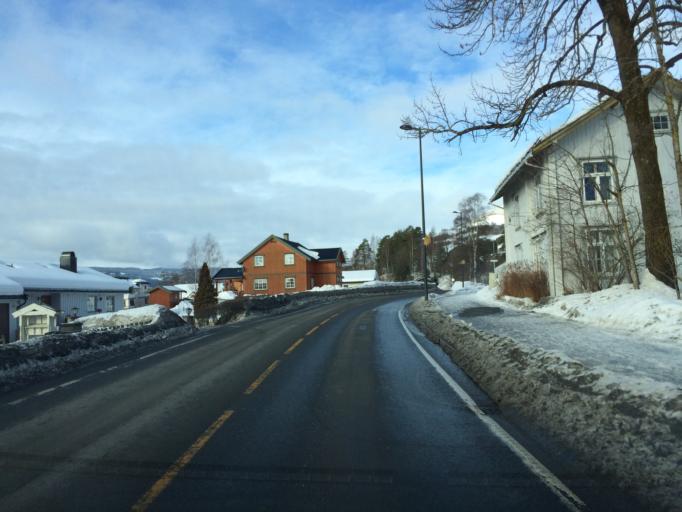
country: NO
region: Oppland
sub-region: Gausdal
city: Segalstad bru
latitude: 61.2168
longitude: 10.2791
